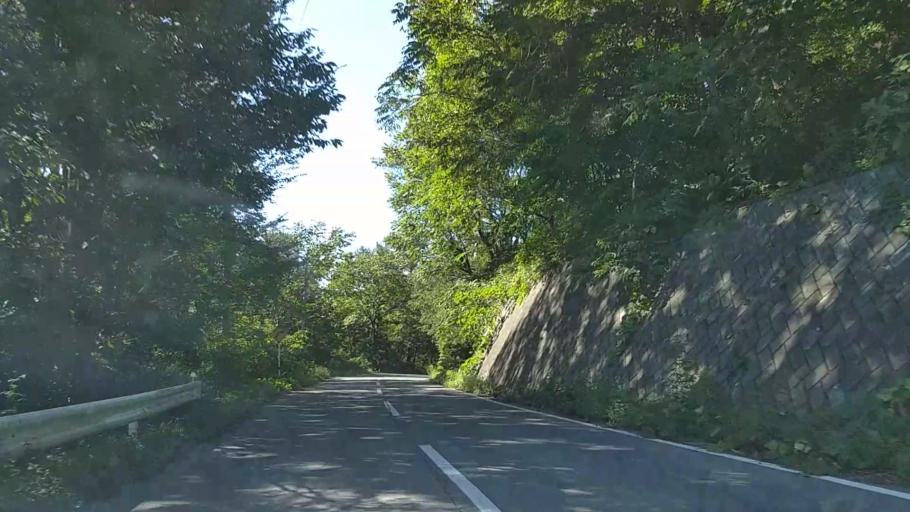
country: JP
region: Nagano
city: Nagano-shi
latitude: 36.6066
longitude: 138.0918
